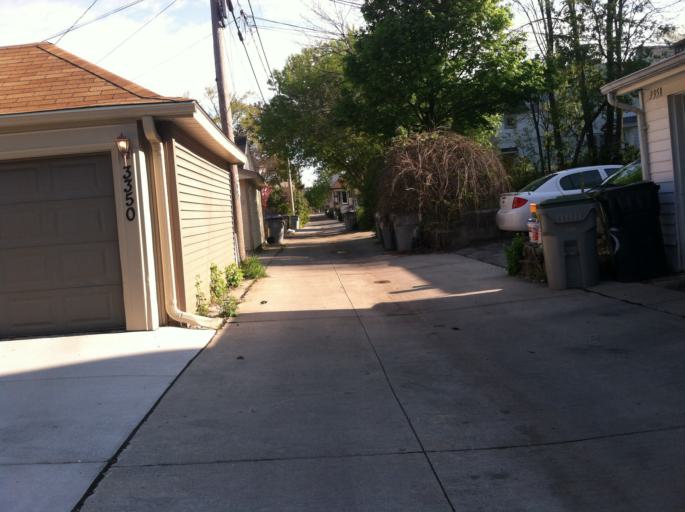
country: US
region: Wisconsin
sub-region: Milwaukee County
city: Shorewood
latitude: 43.0787
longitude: -87.8897
